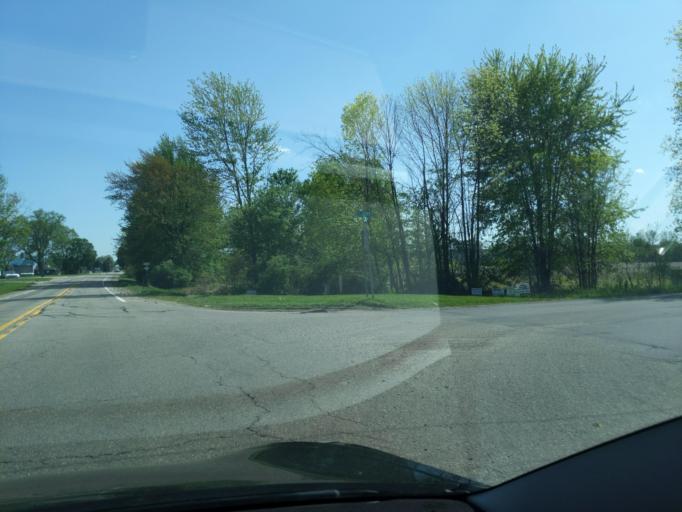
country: US
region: Michigan
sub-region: Kent County
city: Lowell
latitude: 42.8567
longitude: -85.3708
